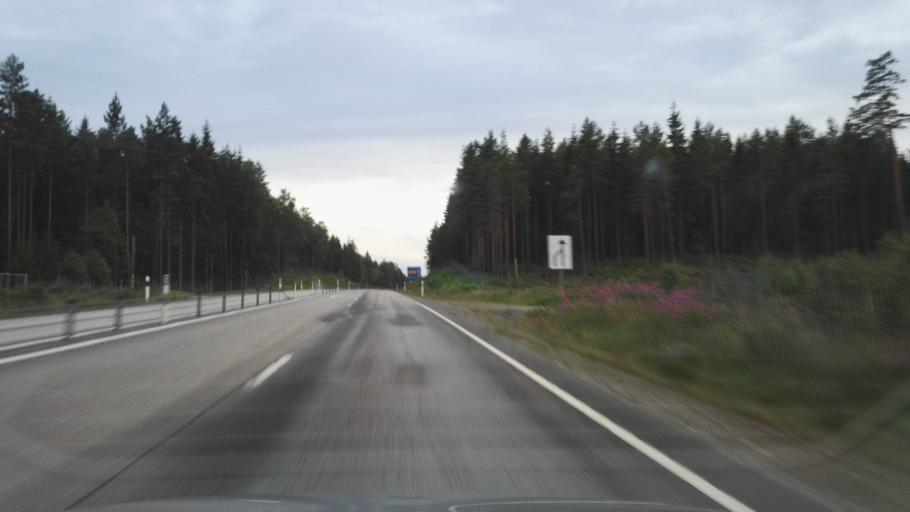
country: SE
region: Kronoberg
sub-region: Vaxjo Kommun
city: Braas
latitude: 57.0100
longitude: 15.0465
